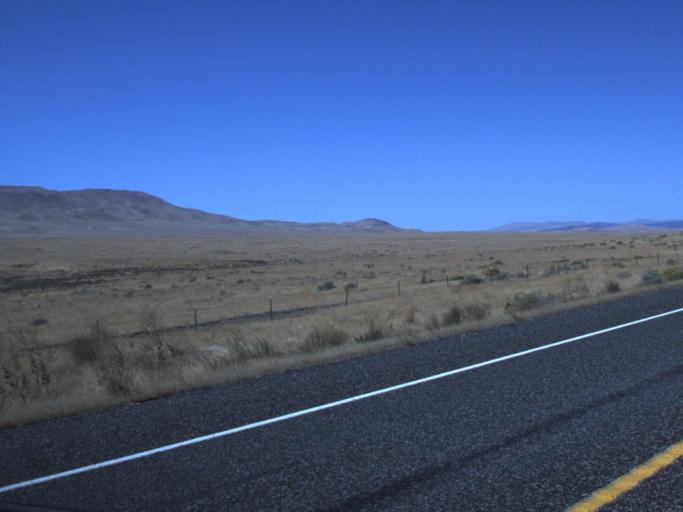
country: US
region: Washington
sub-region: Benton County
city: West Richland
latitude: 46.4175
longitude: -119.4614
